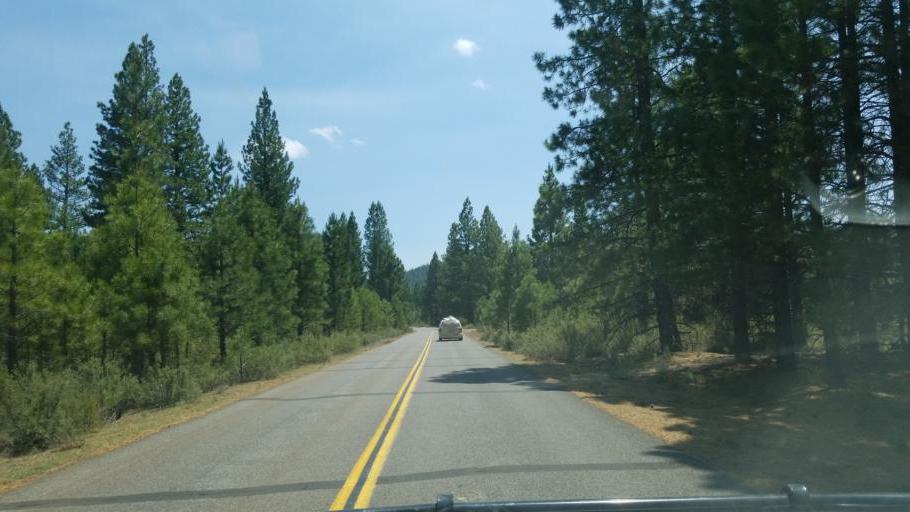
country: US
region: California
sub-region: Lassen County
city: Susanville
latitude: 40.5711
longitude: -120.8436
